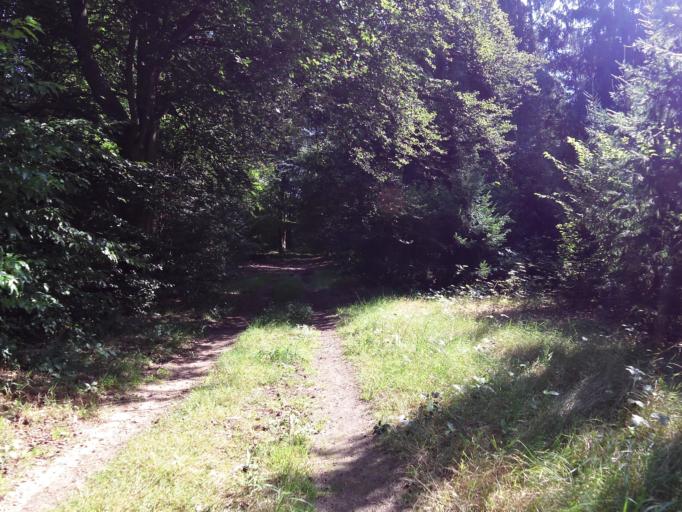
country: DE
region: Hesse
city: Morfelden-Walldorf
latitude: 50.0029
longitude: 8.6063
